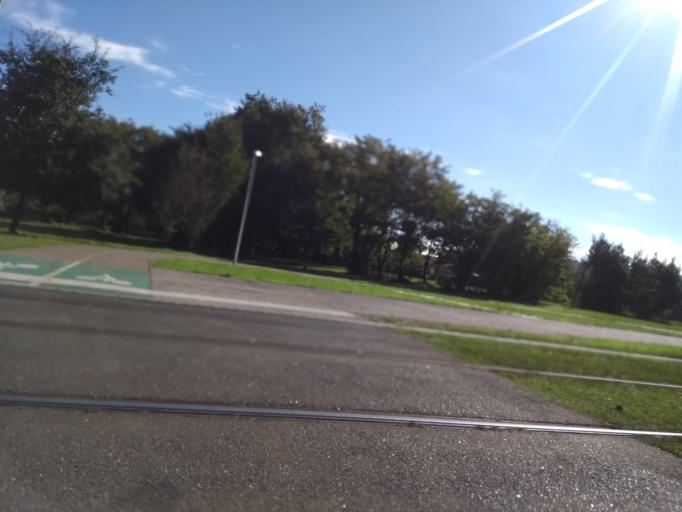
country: FR
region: Aquitaine
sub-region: Departement de la Gironde
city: Pessac
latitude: 44.7983
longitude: -0.6348
